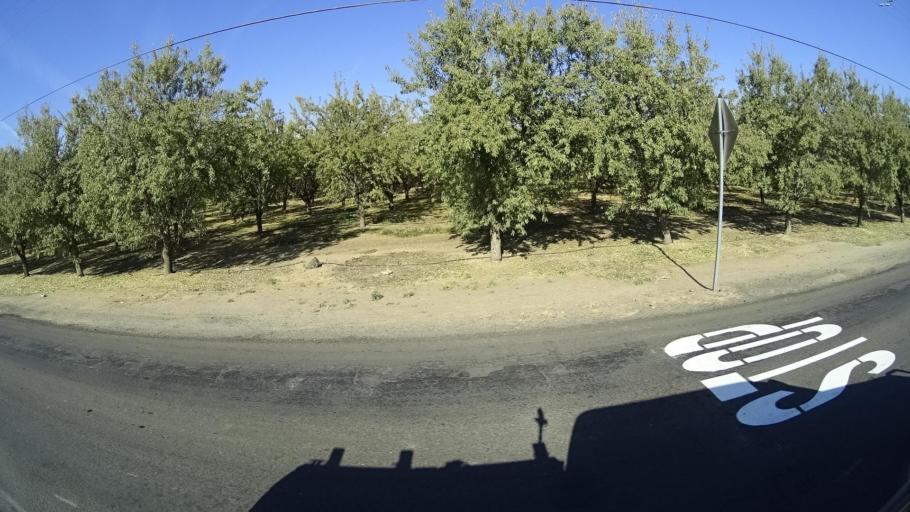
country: US
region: California
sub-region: Kern County
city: McFarland
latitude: 35.6890
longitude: -119.2207
